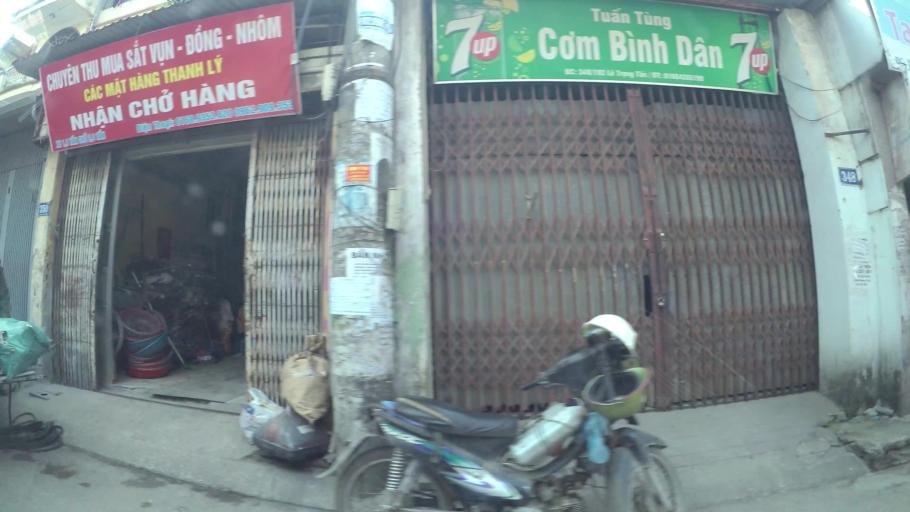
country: VN
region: Ha Noi
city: Thanh Xuan
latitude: 20.9853
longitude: 105.8243
